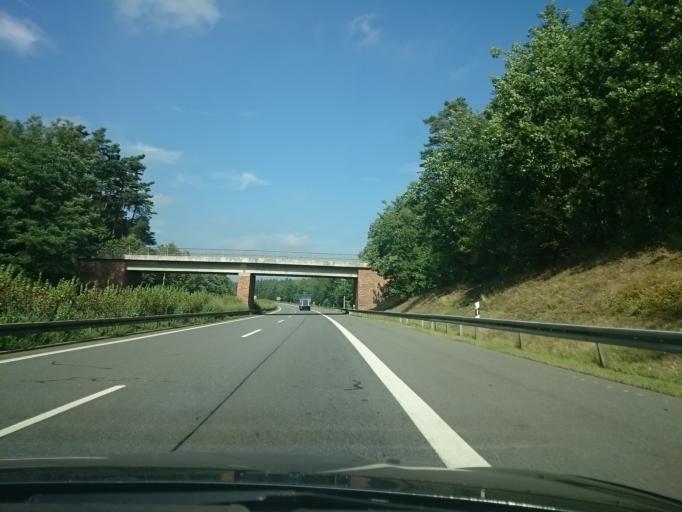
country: DE
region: Brandenburg
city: Bronkow
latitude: 51.6529
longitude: 13.9381
